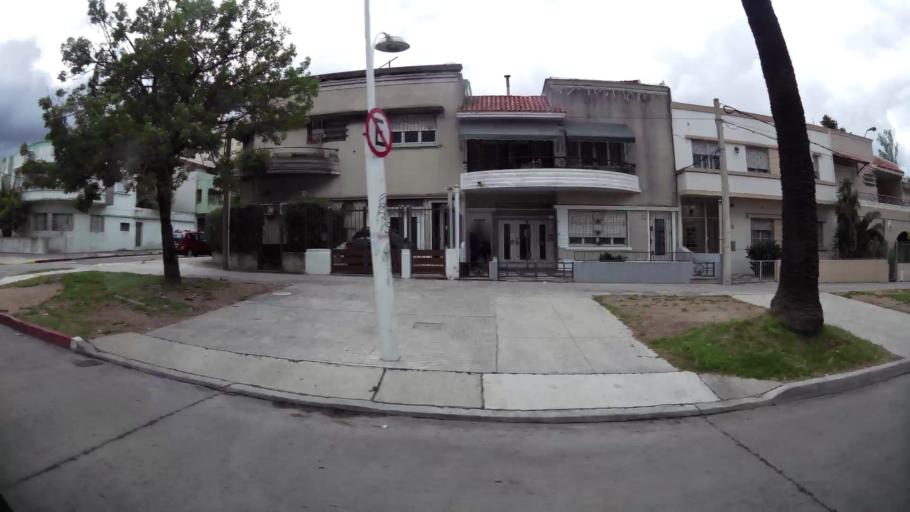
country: UY
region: Montevideo
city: Montevideo
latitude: -34.8709
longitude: -56.1675
